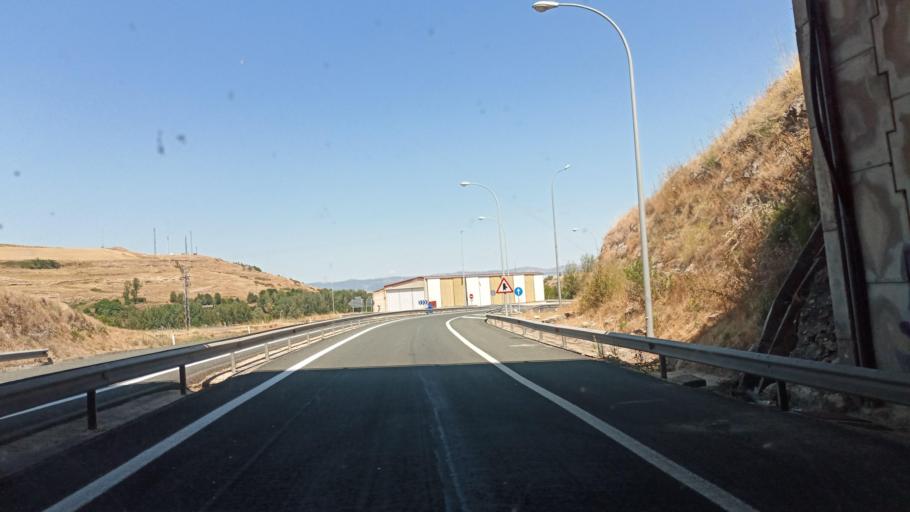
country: ES
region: Castille and Leon
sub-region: Provincia de Burgos
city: Briviesca
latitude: 42.5322
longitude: -3.3203
